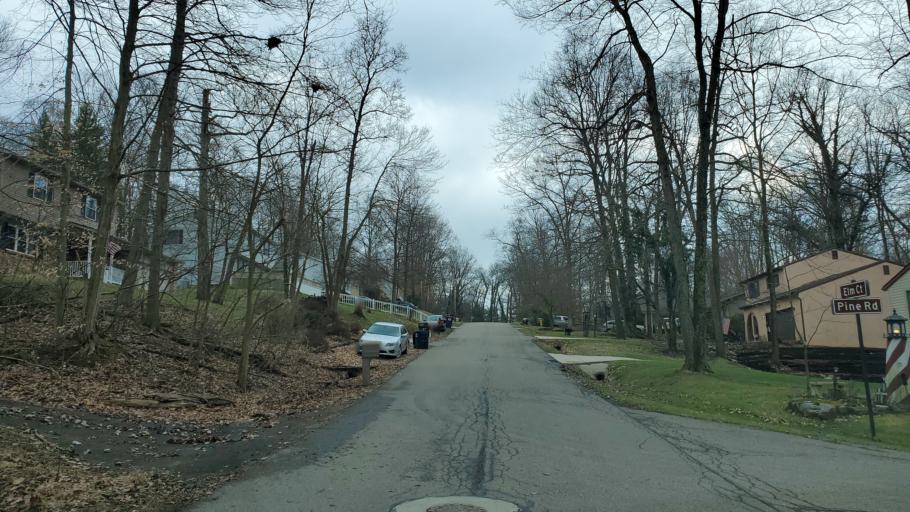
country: US
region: Ohio
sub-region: Licking County
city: Newark
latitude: 40.0259
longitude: -82.3775
